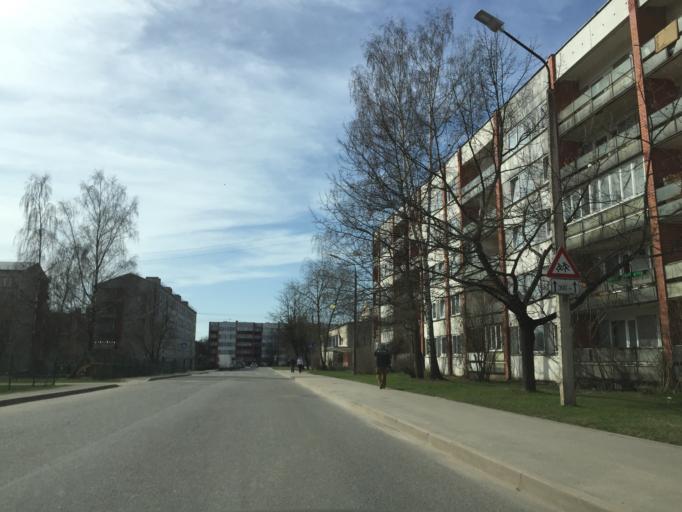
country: LV
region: Ogre
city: Ogre
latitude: 56.8164
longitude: 24.5959
